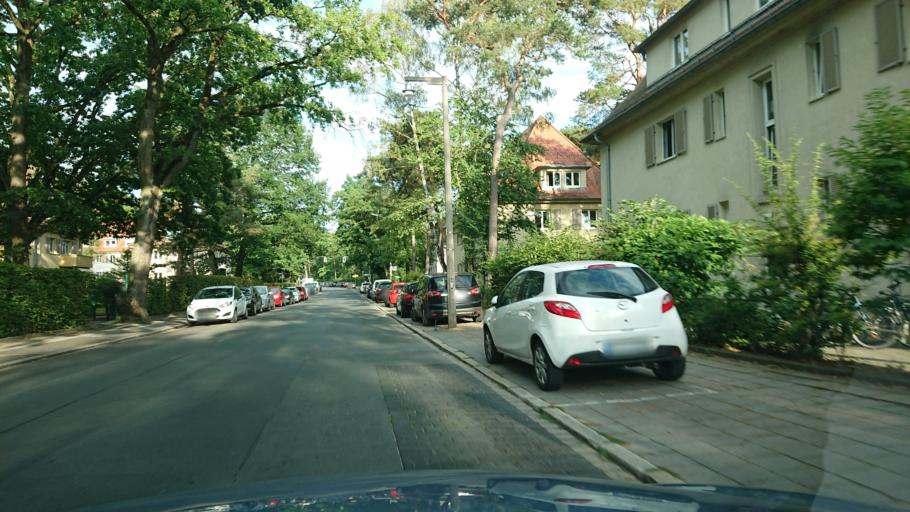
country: DE
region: Bavaria
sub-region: Regierungsbezirk Mittelfranken
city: Erlangen
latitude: 49.6042
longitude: 11.0204
